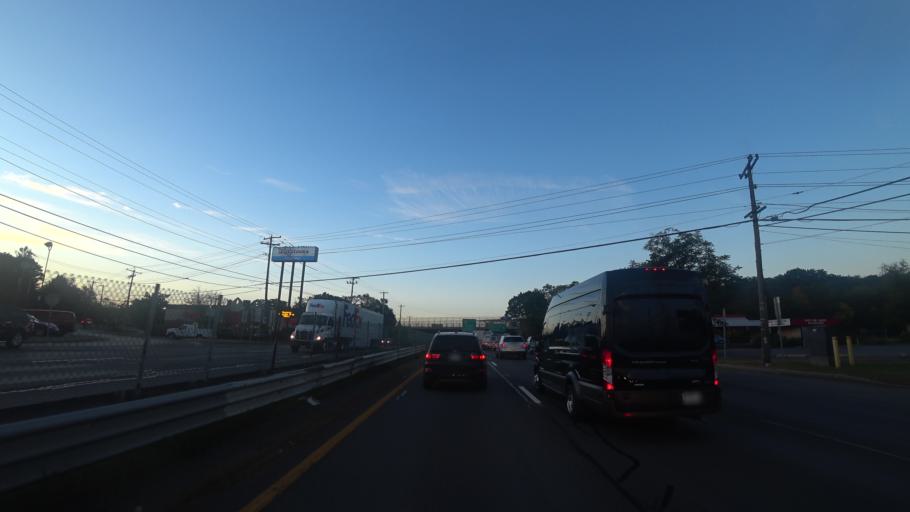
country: US
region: Massachusetts
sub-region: Essex County
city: Saugus
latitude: 42.4584
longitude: -71.0240
